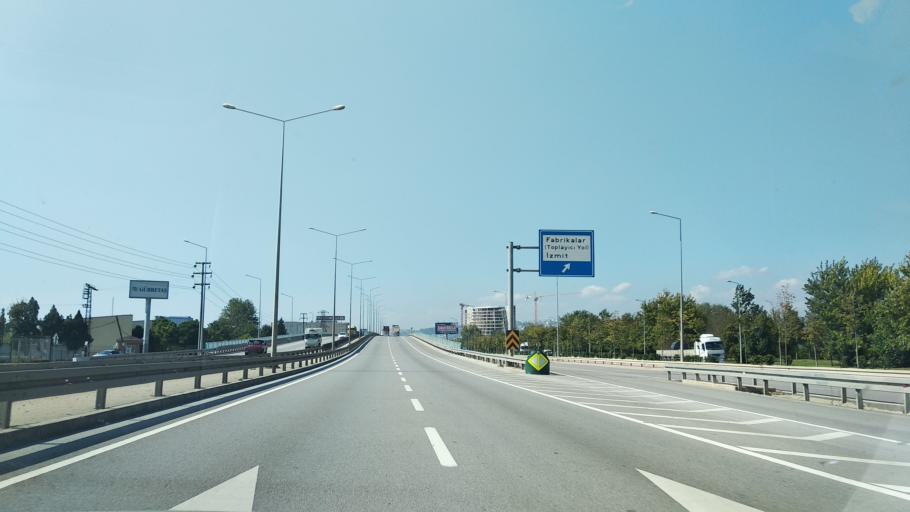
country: TR
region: Kocaeli
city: Kosekoy
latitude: 40.7580
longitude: 29.9919
